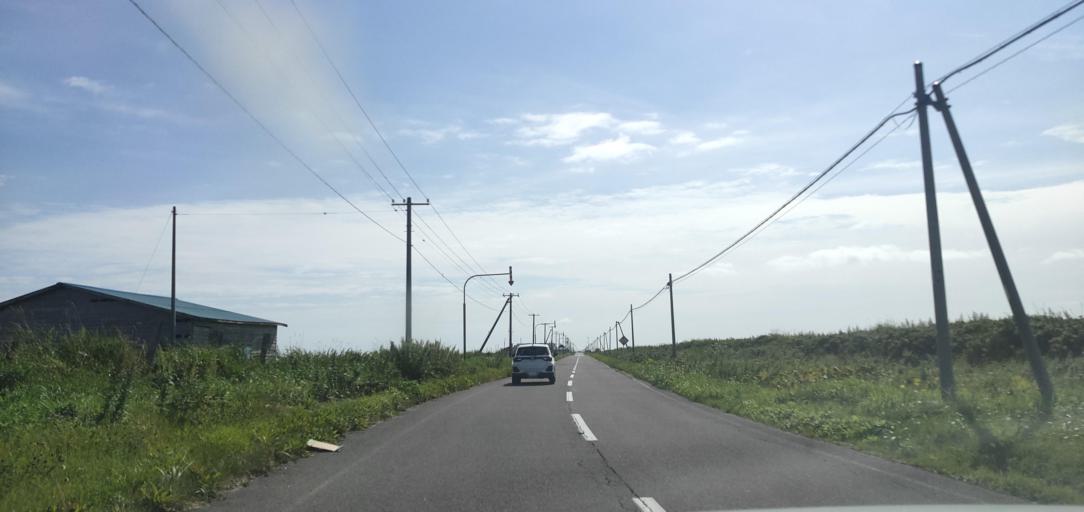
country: JP
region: Hokkaido
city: Shibetsu
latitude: 43.6373
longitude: 145.1687
